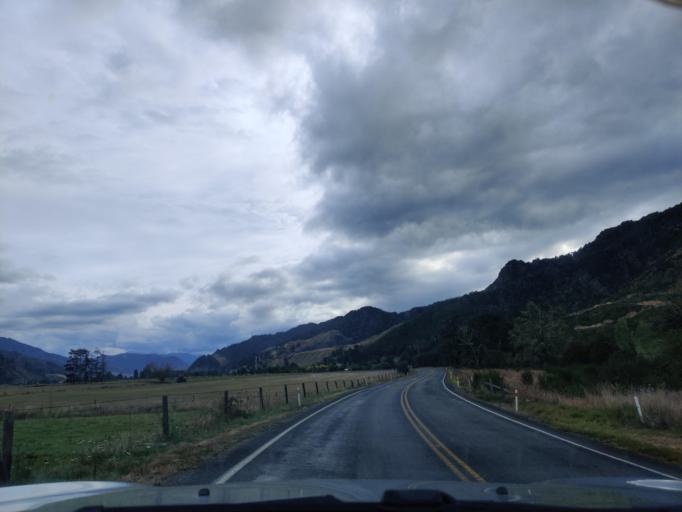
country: NZ
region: Tasman
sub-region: Tasman District
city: Wakefield
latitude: -41.7591
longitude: 172.3875
